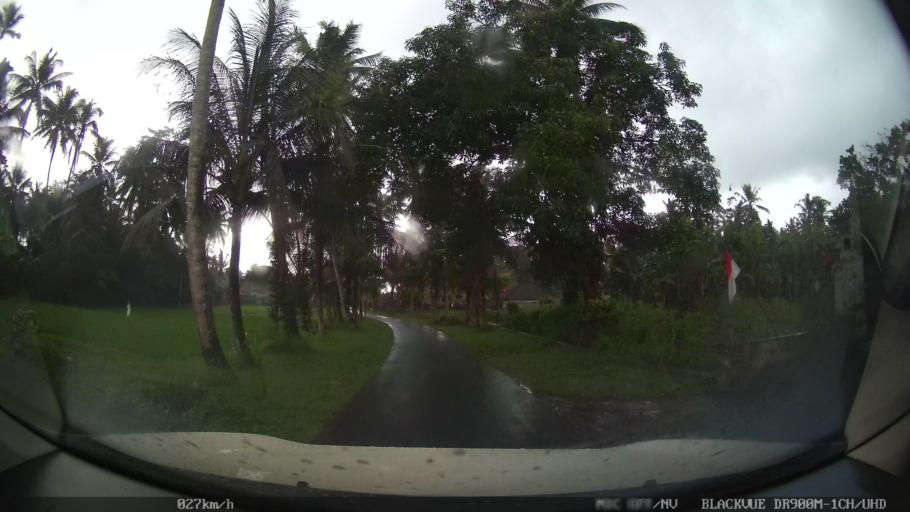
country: ID
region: Bali
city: Kekeran
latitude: -8.4886
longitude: 115.1876
